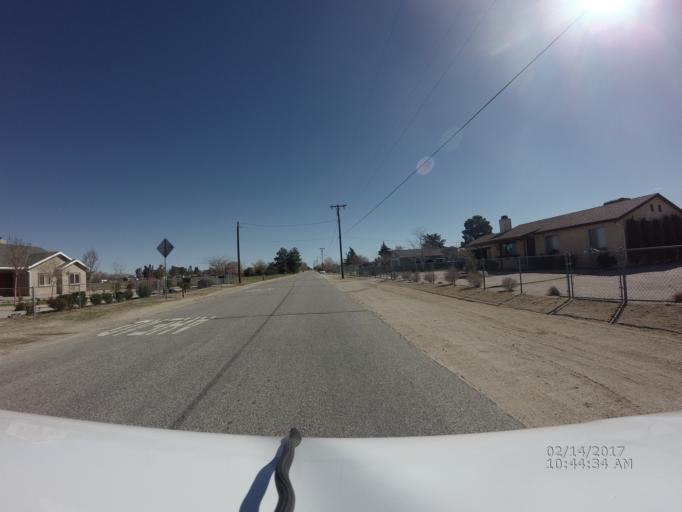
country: US
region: California
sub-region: Los Angeles County
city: Littlerock
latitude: 34.5670
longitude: -117.9417
